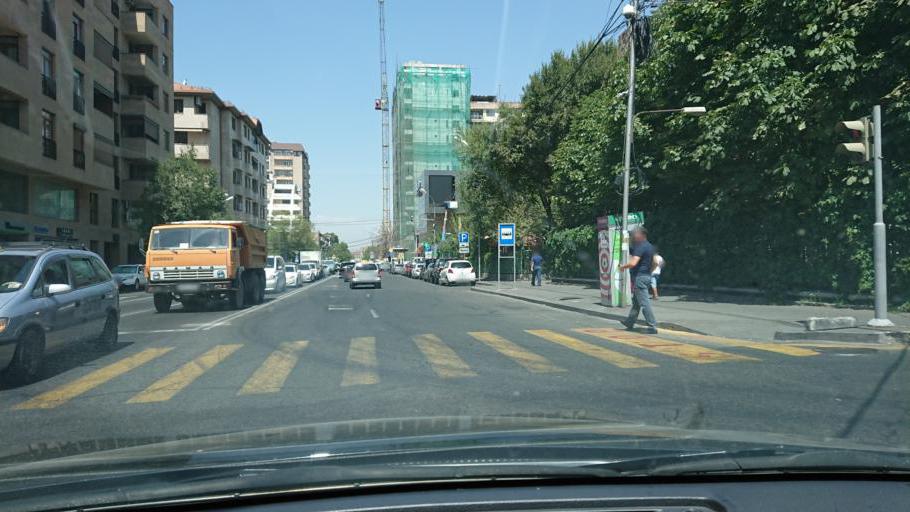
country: AM
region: Yerevan
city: Yerevan
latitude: 40.1987
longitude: 44.5016
